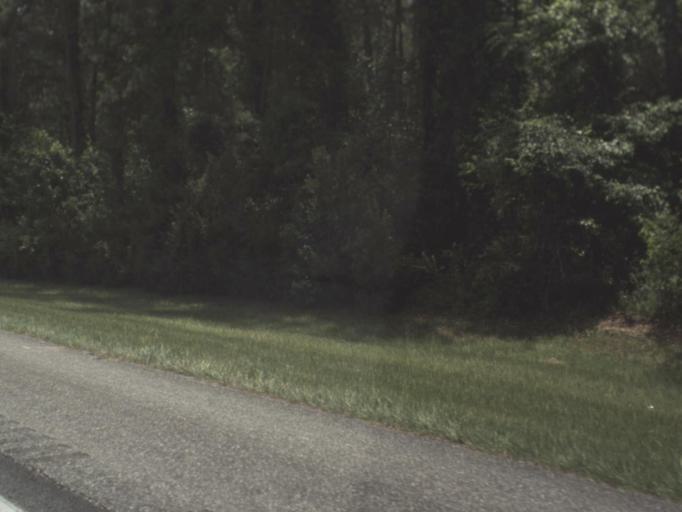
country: US
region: Florida
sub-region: Madison County
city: Madison
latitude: 30.4352
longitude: -83.6395
